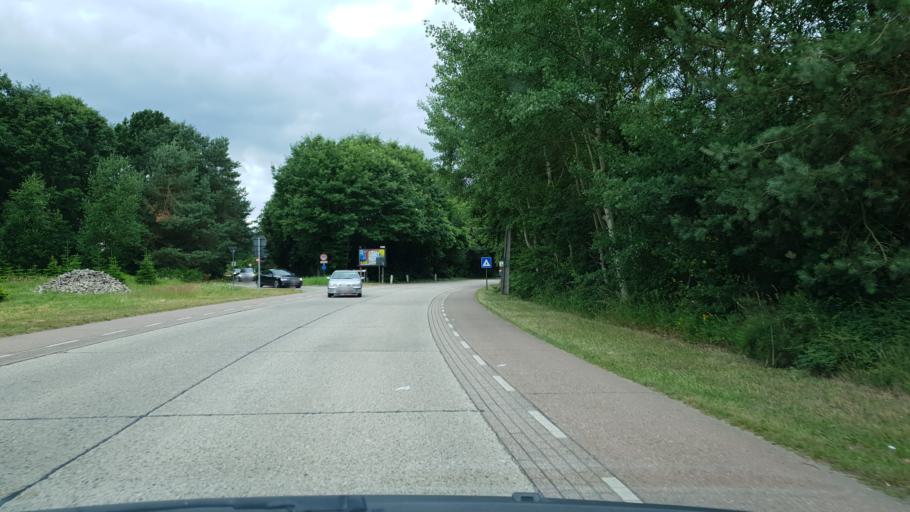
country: BE
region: Flanders
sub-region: Provincie Antwerpen
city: Westerlo
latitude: 51.0856
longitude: 4.8845
